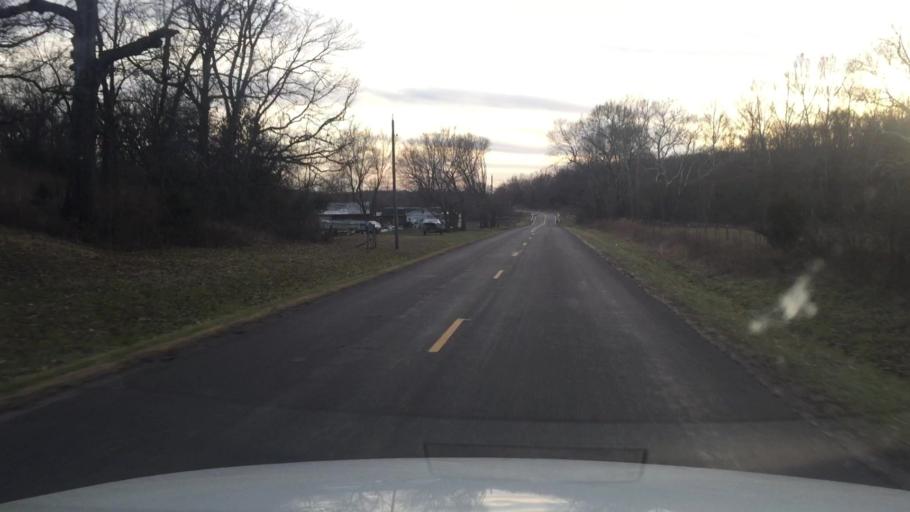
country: US
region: Missouri
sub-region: Miller County
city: Eldon
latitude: 38.3645
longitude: -92.6843
